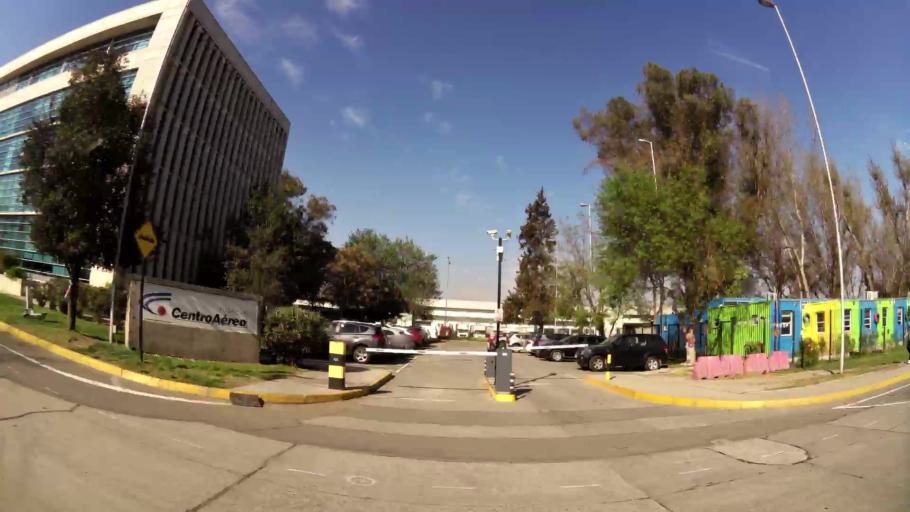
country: CL
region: Santiago Metropolitan
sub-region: Provincia de Santiago
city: Lo Prado
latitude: -33.4056
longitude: -70.7918
